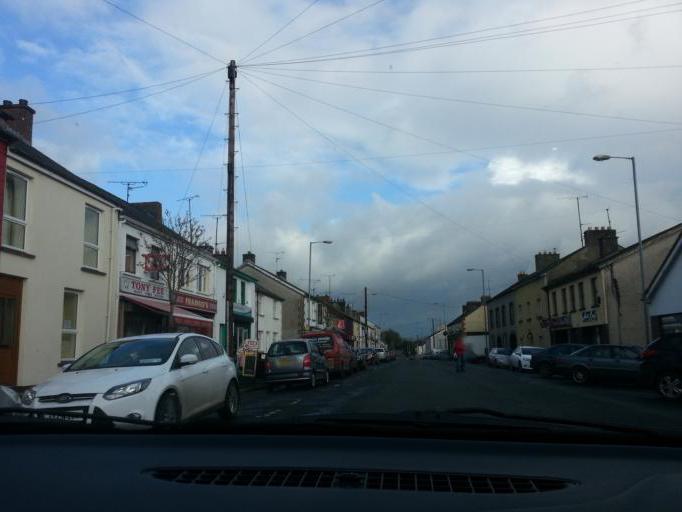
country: GB
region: Northern Ireland
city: Lisnaskea
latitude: 54.1822
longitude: -7.3601
